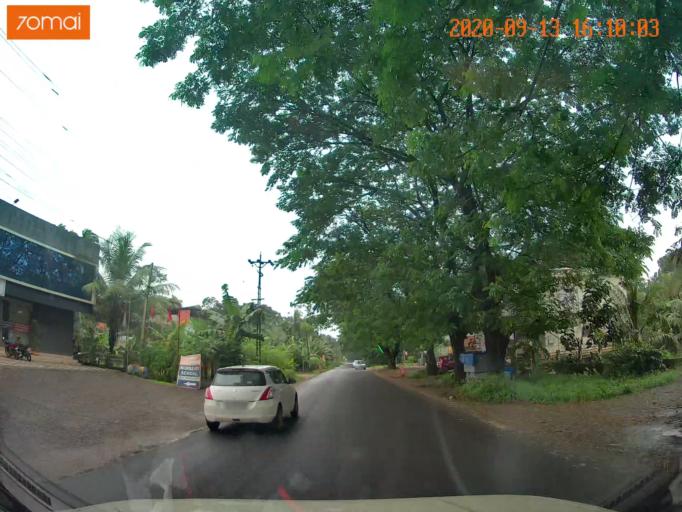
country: IN
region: Kerala
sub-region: Kottayam
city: Palackattumala
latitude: 9.6795
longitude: 76.6034
